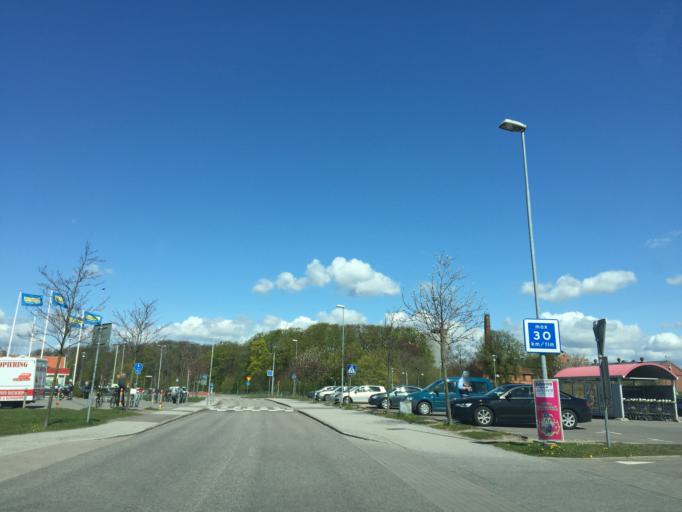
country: SE
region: Skane
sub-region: Staffanstorps Kommun
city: Staffanstorp
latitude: 55.6397
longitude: 13.2167
